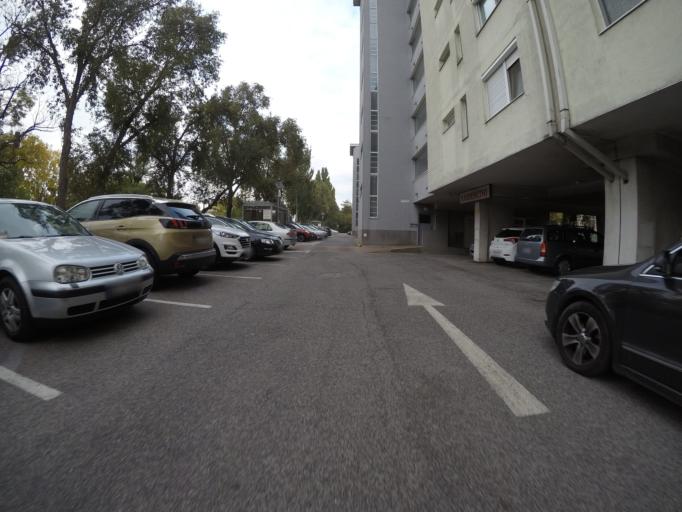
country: SK
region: Bratislavsky
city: Bratislava
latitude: 48.1637
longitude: 17.1720
